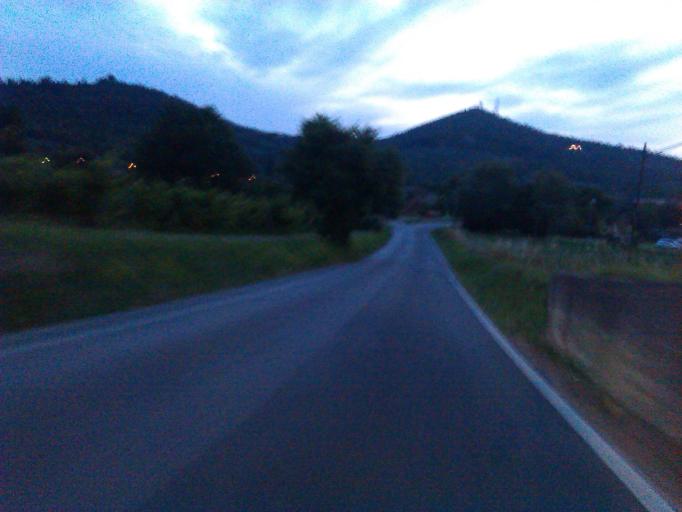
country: IT
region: Tuscany
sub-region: Province of Arezzo
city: Battifolle-Ruscello-Poggiola
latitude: 43.4499
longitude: 11.7938
